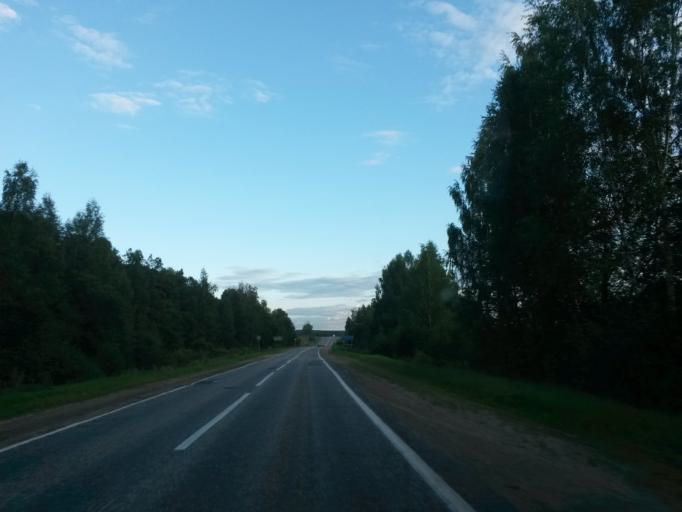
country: RU
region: Jaroslavl
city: Krasnyye Tkachi
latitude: 57.4527
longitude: 39.9125
